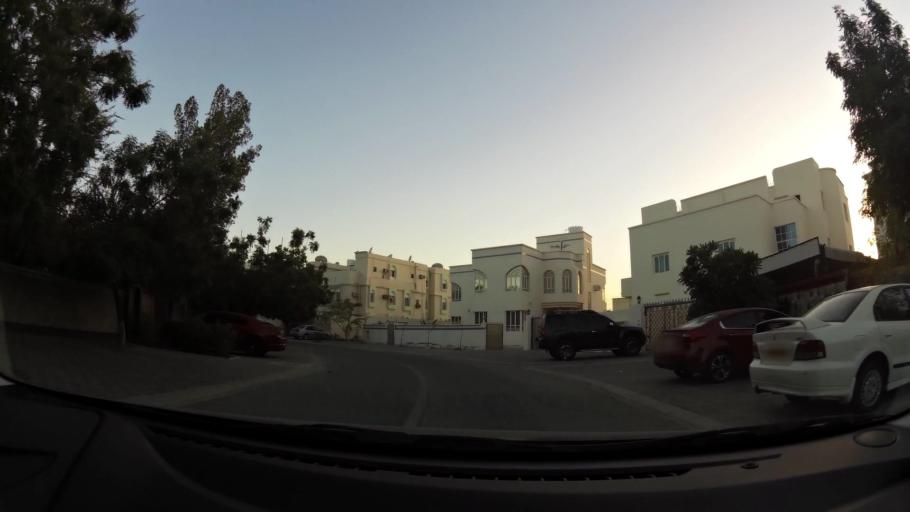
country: OM
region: Muhafazat Masqat
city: As Sib al Jadidah
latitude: 23.5971
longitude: 58.2343
